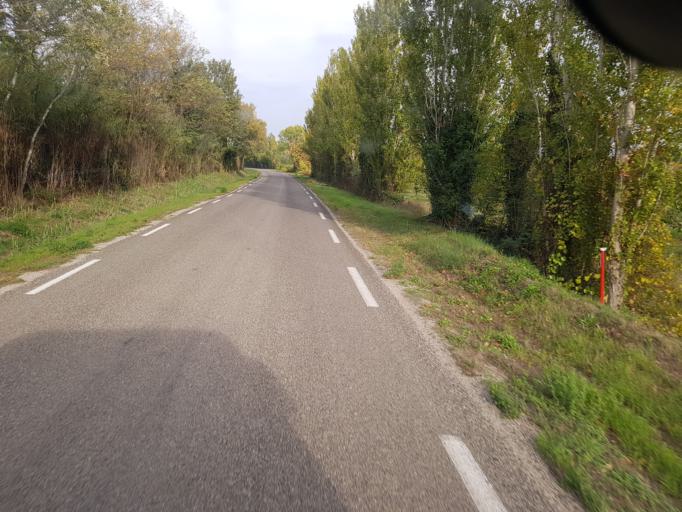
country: FR
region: Languedoc-Roussillon
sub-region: Departement du Gard
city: Vallabregues
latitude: 43.8669
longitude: 4.6489
